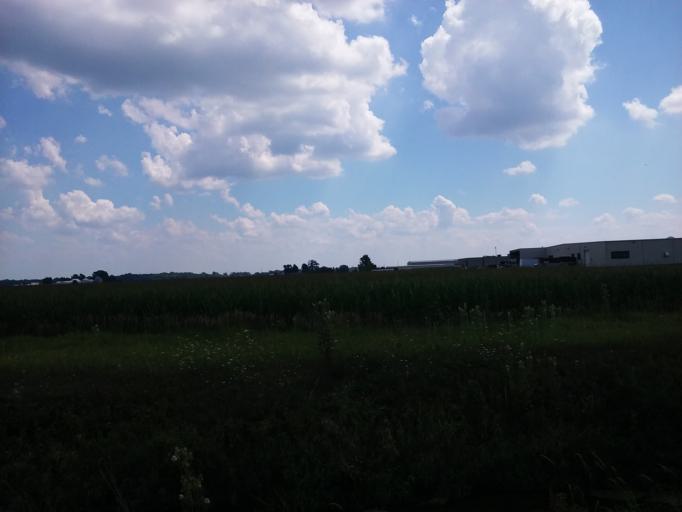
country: US
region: Ohio
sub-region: Wood County
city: Bowling Green
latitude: 41.3850
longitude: -83.6010
